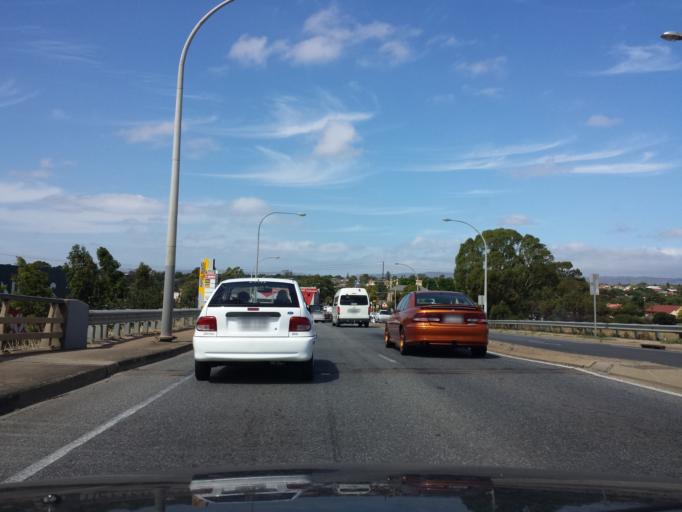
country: AU
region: South Australia
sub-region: Prospect
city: Prospect
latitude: -34.8746
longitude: 138.5818
